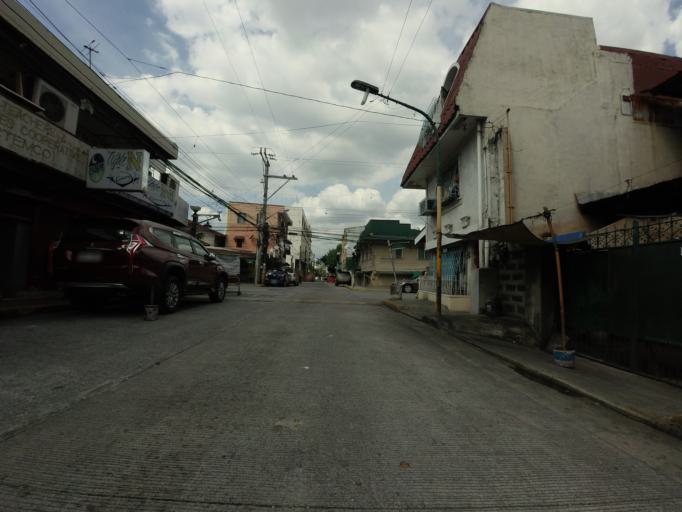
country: PH
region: Metro Manila
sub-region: City of Manila
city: Quiapo
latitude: 14.5707
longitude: 121.0032
